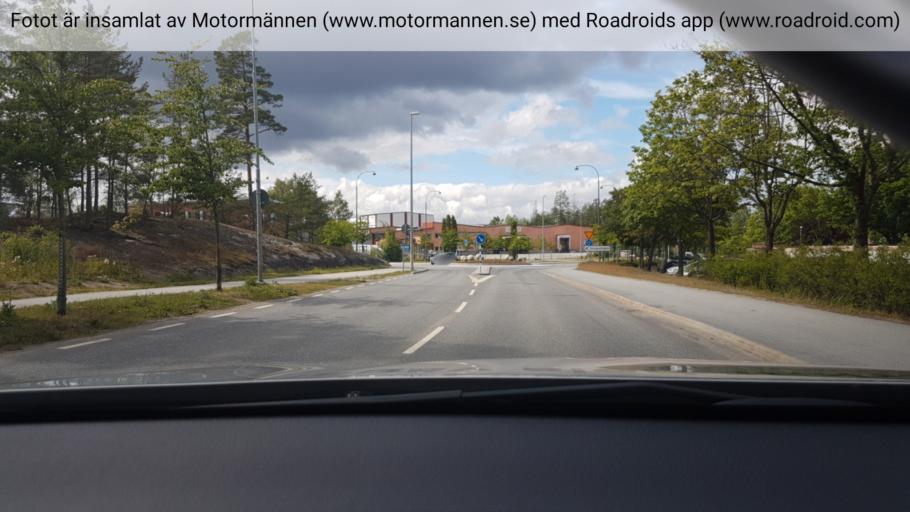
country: SE
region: Stockholm
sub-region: Tyreso Kommun
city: Bollmora
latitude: 59.2397
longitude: 18.2179
